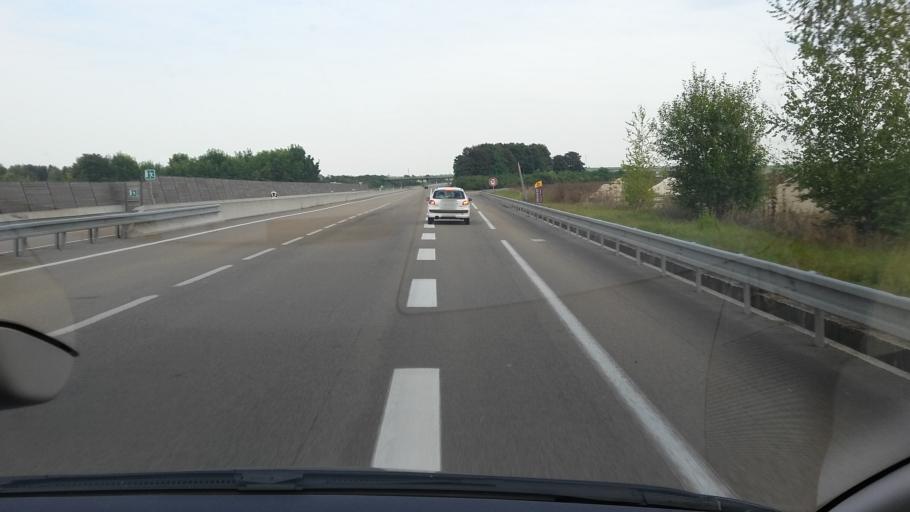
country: FR
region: Champagne-Ardenne
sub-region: Departement de la Marne
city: Fere-Champenoise
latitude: 48.7492
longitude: 3.9950
